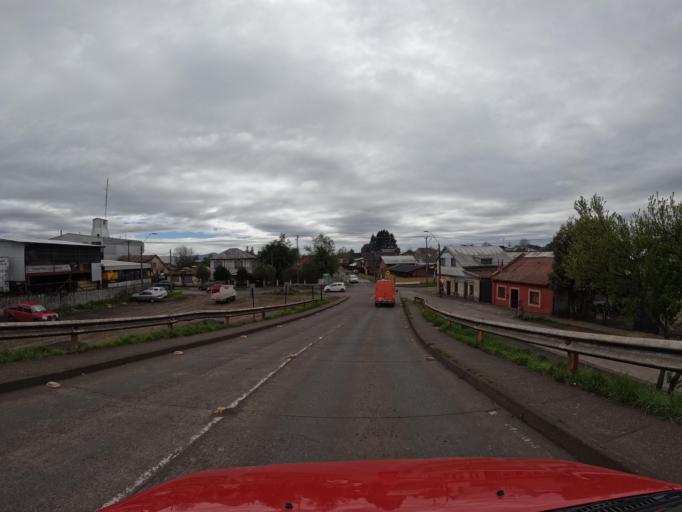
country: CL
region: Araucania
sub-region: Provincia de Malleco
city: Victoria
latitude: -38.2339
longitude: -72.3283
